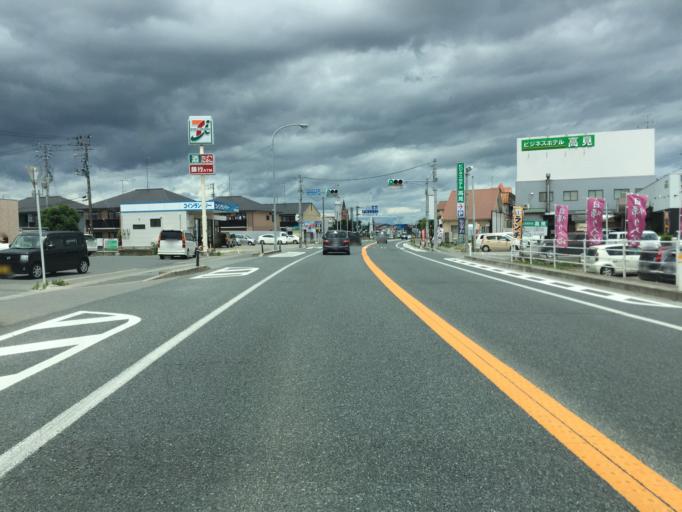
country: JP
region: Fukushima
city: Namie
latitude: 37.6341
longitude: 140.9848
